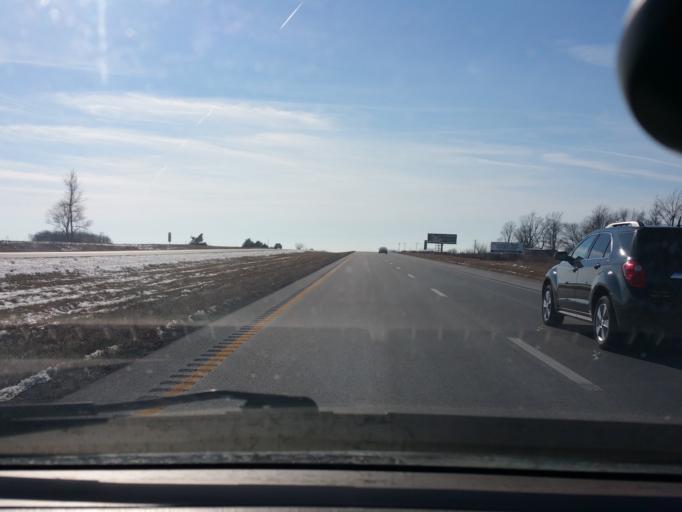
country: US
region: Missouri
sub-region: Clinton County
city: Cameron
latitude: 39.8369
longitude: -94.1843
